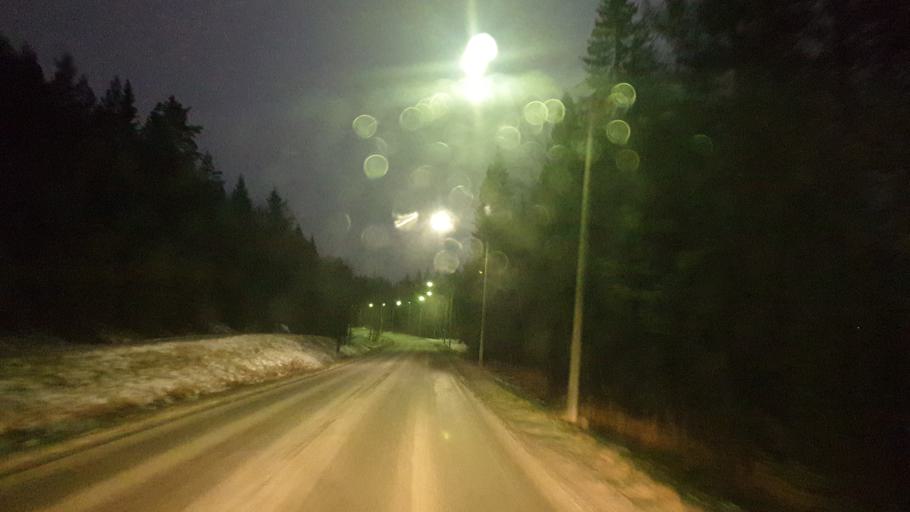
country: FI
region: Southern Savonia
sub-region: Savonlinna
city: Savonlinna
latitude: 61.8634
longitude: 28.9444
